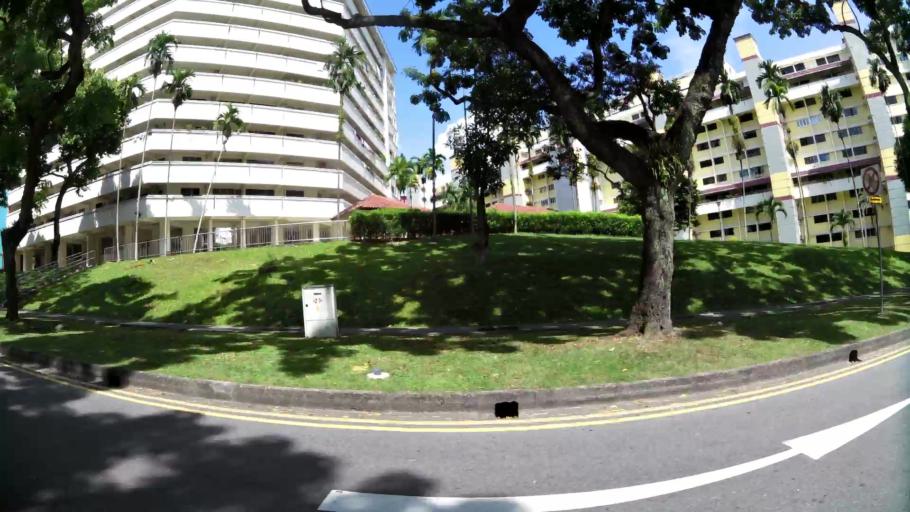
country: SG
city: Singapore
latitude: 1.3751
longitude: 103.8383
